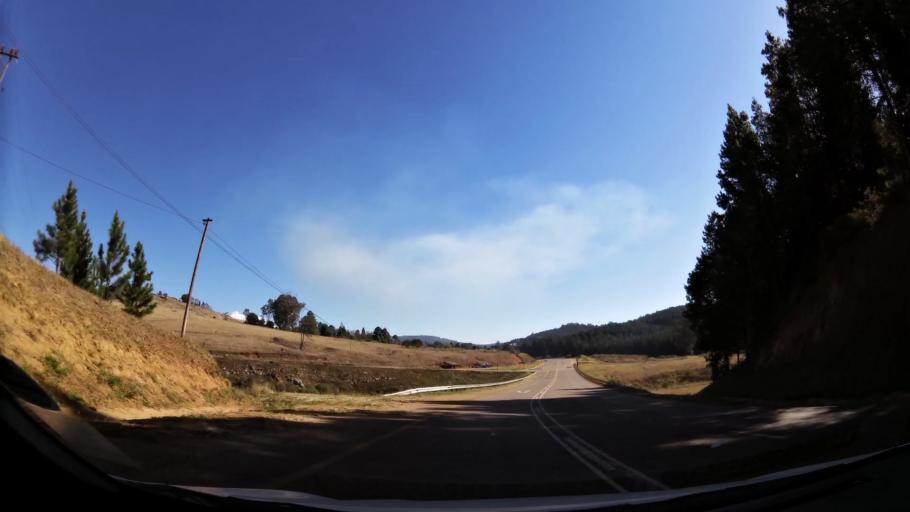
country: ZA
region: Limpopo
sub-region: Capricorn District Municipality
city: Mankoeng
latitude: -23.9397
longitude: 29.9492
